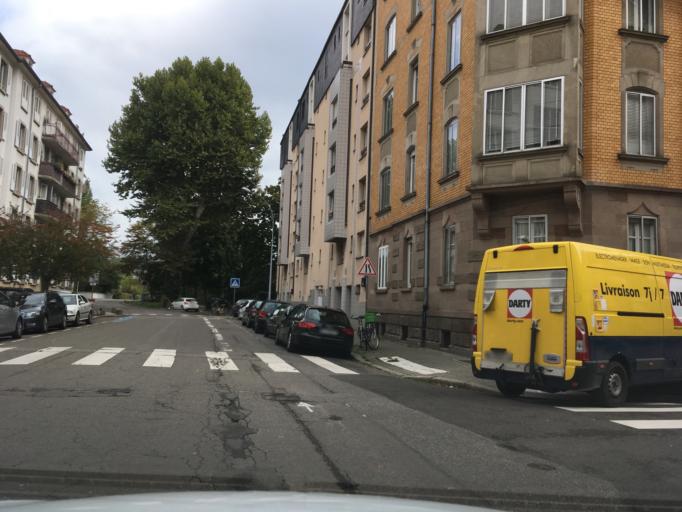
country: FR
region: Alsace
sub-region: Departement du Bas-Rhin
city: Schiltigheim
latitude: 48.5938
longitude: 7.7623
